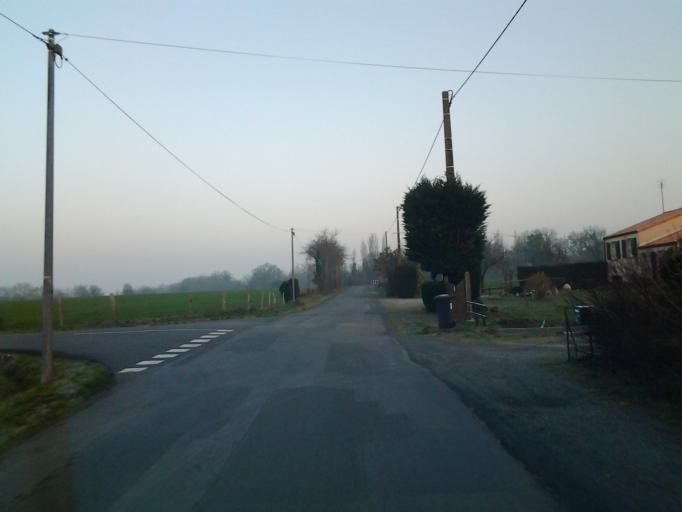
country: FR
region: Pays de la Loire
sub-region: Departement de la Vendee
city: La Chaize-le-Vicomte
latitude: 46.6633
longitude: -1.2436
